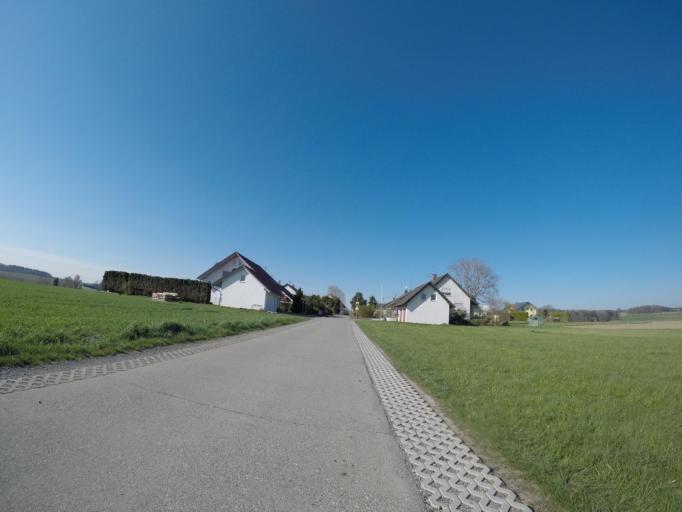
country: DE
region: Baden-Wuerttemberg
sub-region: Tuebingen Region
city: Altshausen
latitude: 47.9244
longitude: 9.5225
